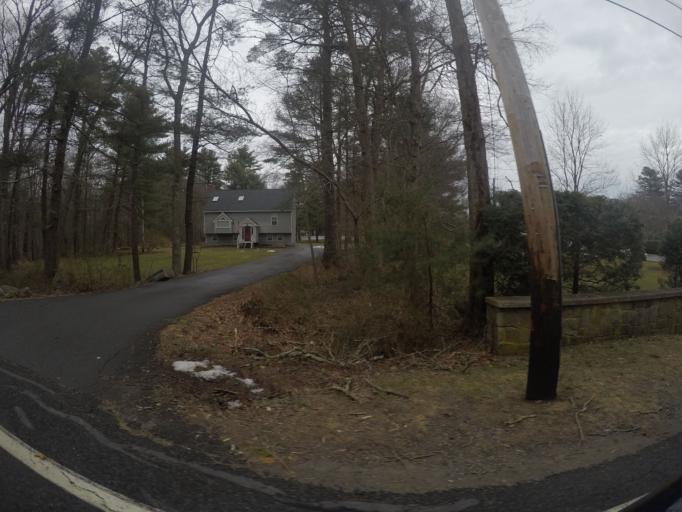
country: US
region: Massachusetts
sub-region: Bristol County
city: Easton
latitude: 42.0435
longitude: -71.1494
